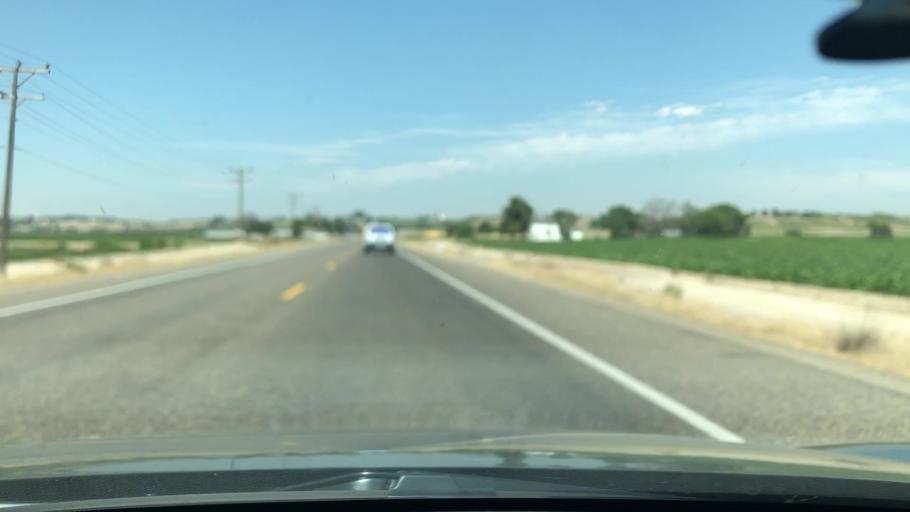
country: US
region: Idaho
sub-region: Owyhee County
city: Homedale
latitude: 43.6422
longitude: -116.9117
